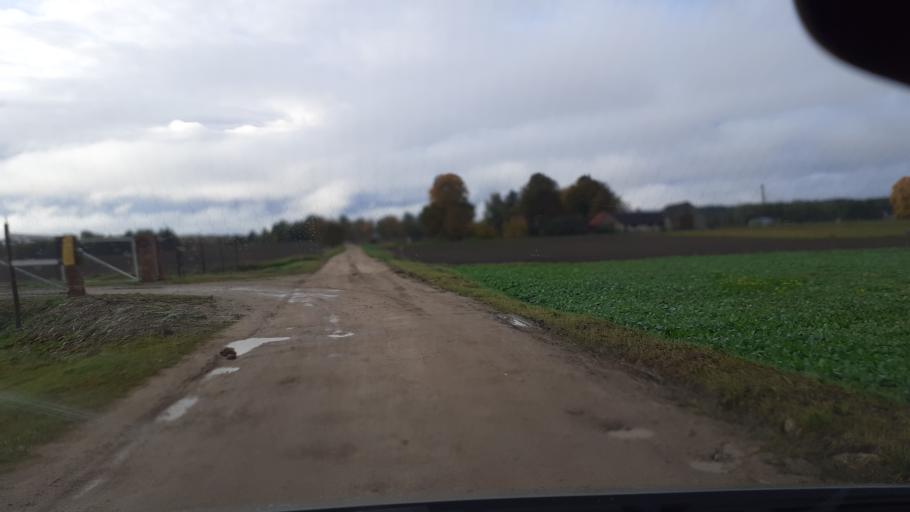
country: LV
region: Kuldigas Rajons
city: Kuldiga
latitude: 56.9789
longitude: 21.9402
